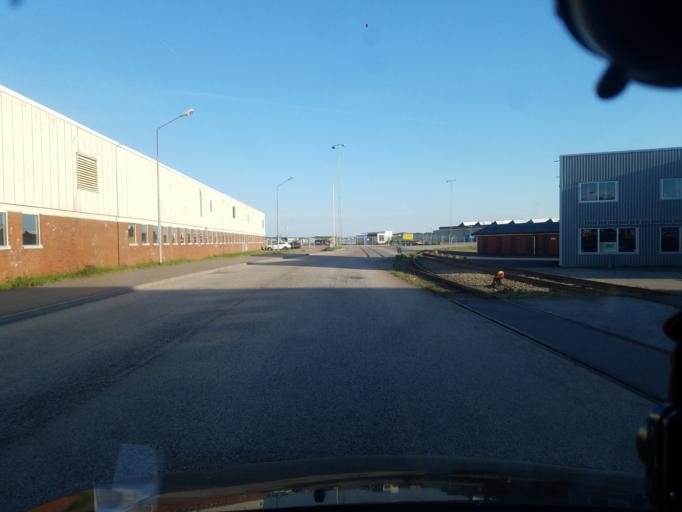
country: SE
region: Vaestra Goetaland
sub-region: Lysekils Kommun
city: Lysekil
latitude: 58.2745
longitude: 11.4536
